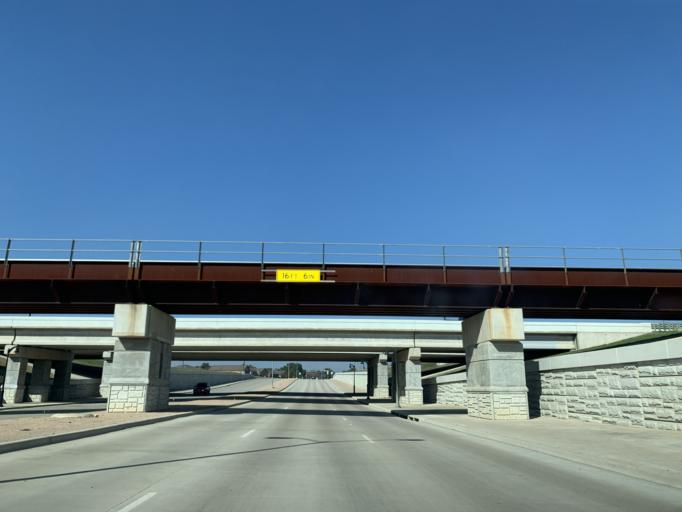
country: US
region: Texas
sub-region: Williamson County
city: Round Rock
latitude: 30.5214
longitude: -97.6395
